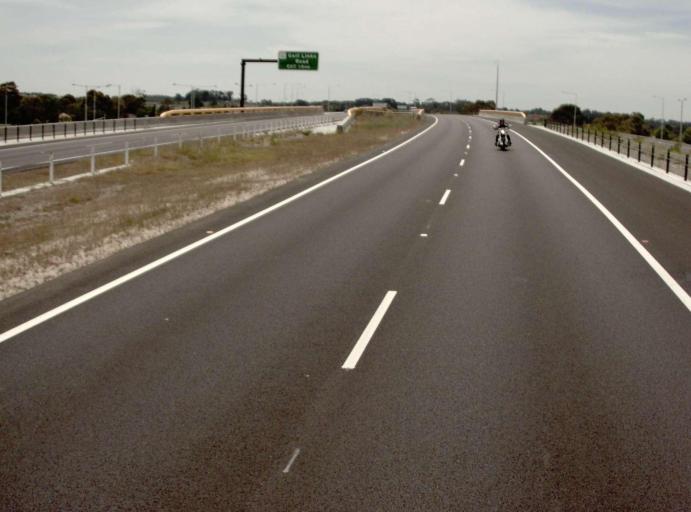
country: AU
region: Victoria
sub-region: Mornington Peninsula
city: Baxter
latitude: -38.1977
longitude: 145.1486
